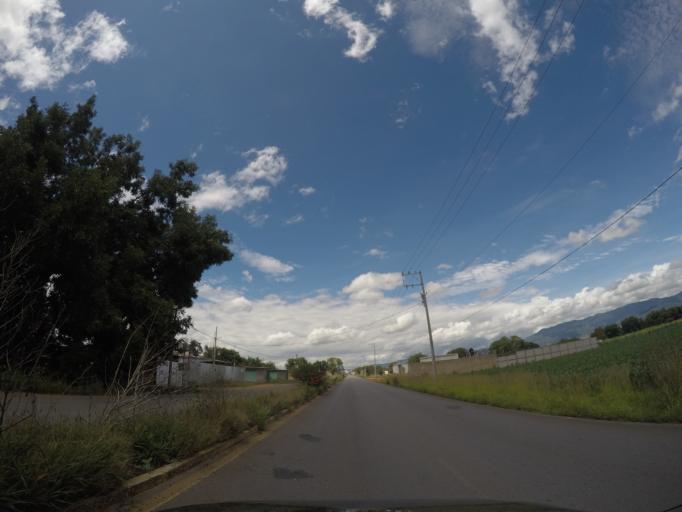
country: MX
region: Oaxaca
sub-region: Santa Cruz Xoxocotlan
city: San Isidro Monjas
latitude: 16.9857
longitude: -96.7467
